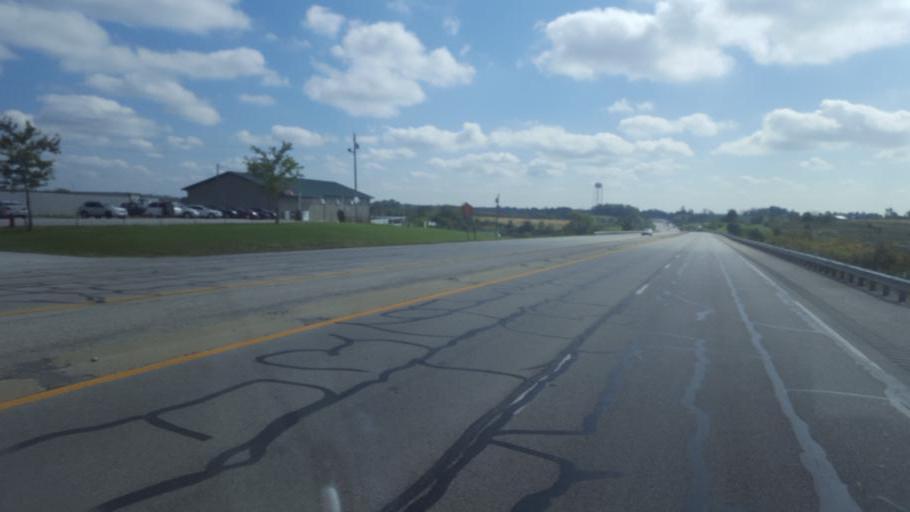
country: US
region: Kentucky
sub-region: Mason County
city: Maysville
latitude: 38.6155
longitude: -83.7776
